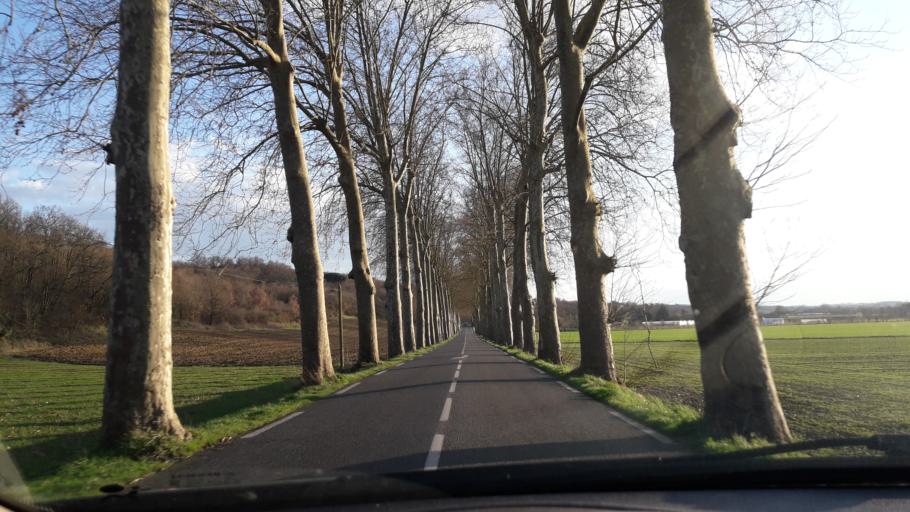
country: FR
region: Midi-Pyrenees
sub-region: Departement de la Haute-Garonne
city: Daux
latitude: 43.7178
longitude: 1.2488
